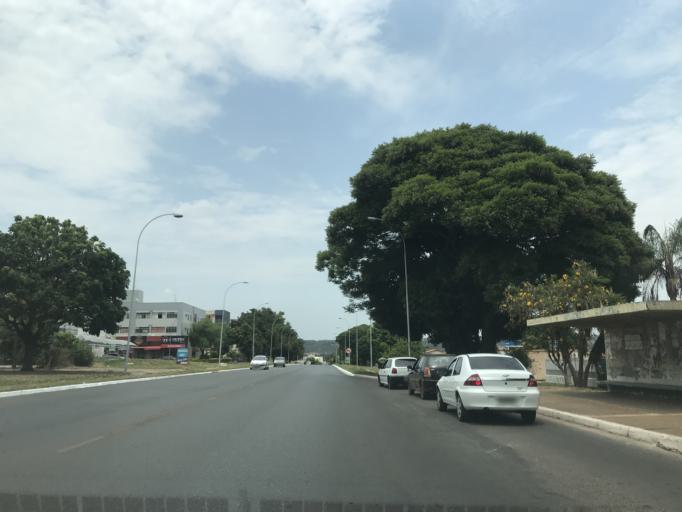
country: BR
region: Federal District
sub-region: Brasilia
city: Brasilia
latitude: -15.6580
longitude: -47.8055
